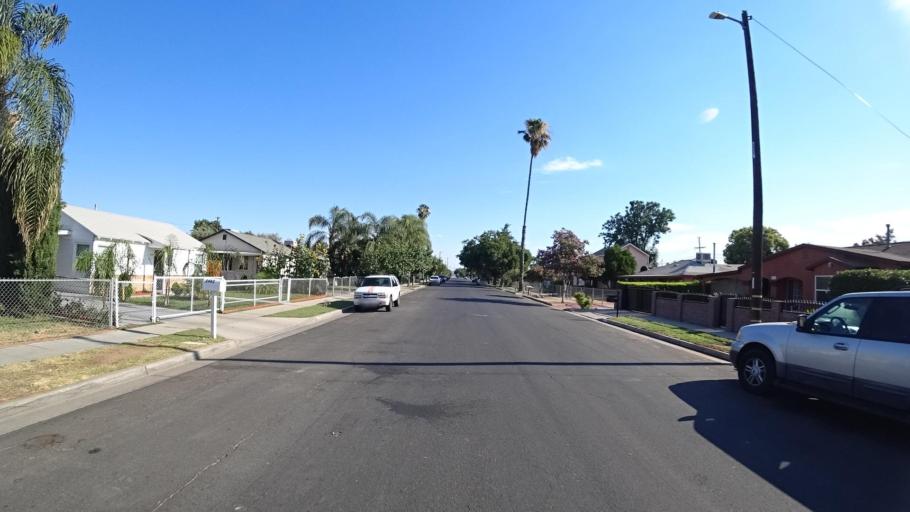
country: US
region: California
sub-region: Fresno County
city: Fresno
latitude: 36.7119
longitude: -119.7416
